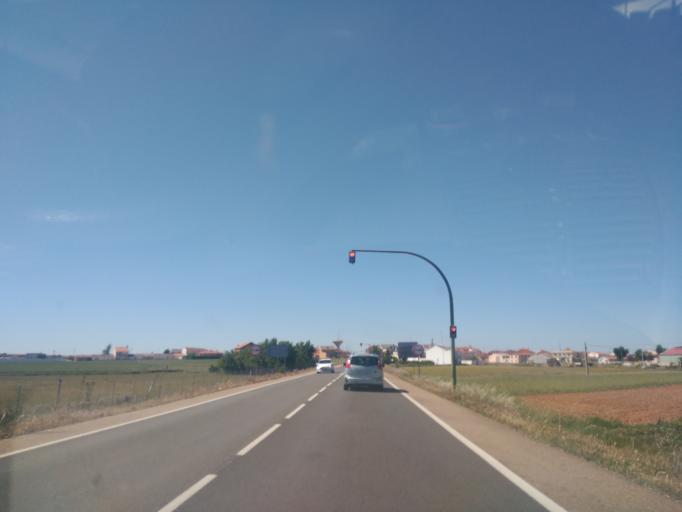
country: ES
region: Castille and Leon
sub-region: Provincia de Salamanca
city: Calvarrasa de Arriba
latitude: 40.9017
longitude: -5.5908
